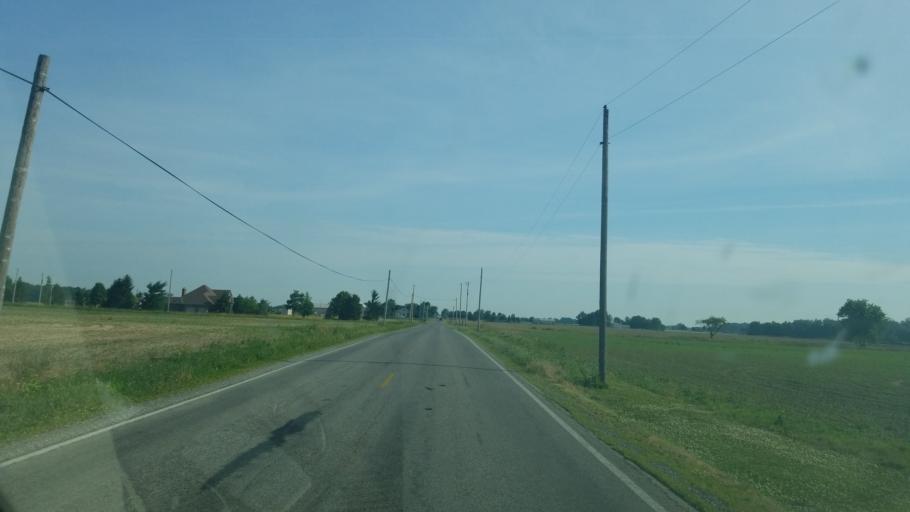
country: US
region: Ohio
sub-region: Hancock County
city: Findlay
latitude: 40.9783
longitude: -83.6985
